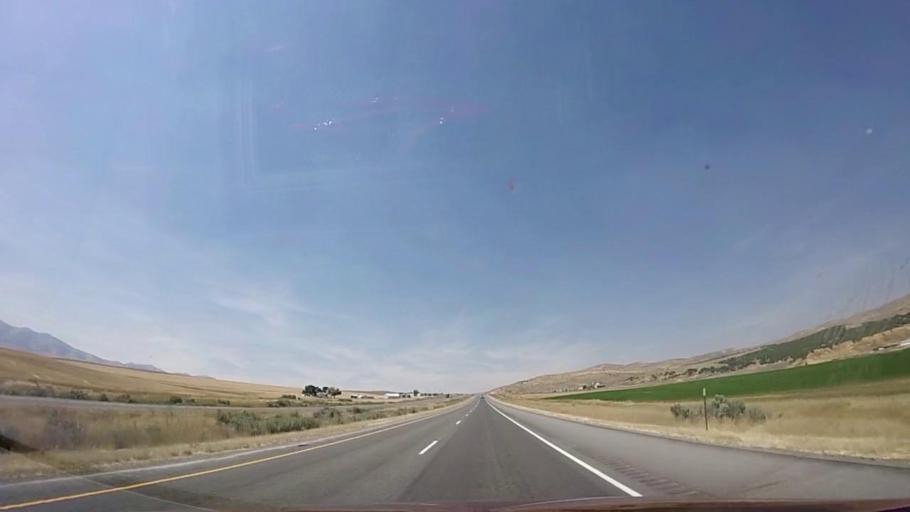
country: US
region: Idaho
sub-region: Power County
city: American Falls
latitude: 42.1650
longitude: -112.9964
